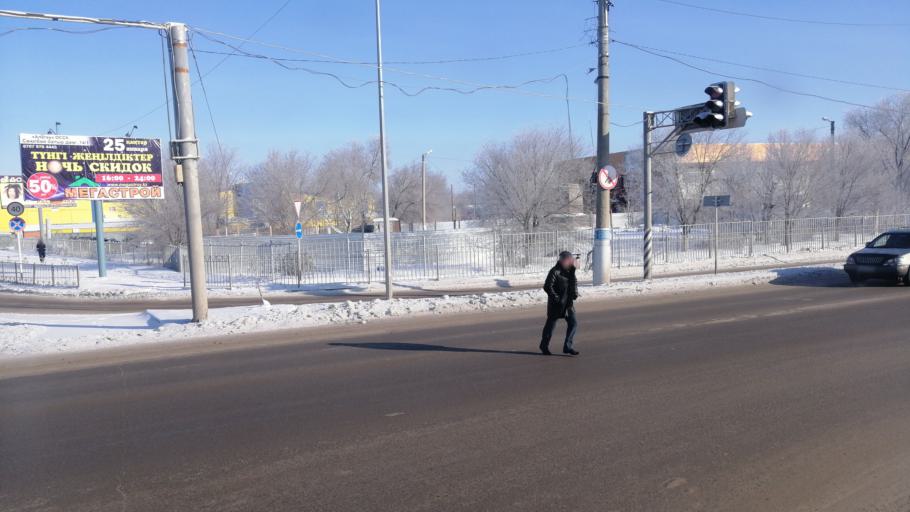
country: KZ
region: Aqtoebe
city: Aqtobe
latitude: 50.2935
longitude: 57.1972
